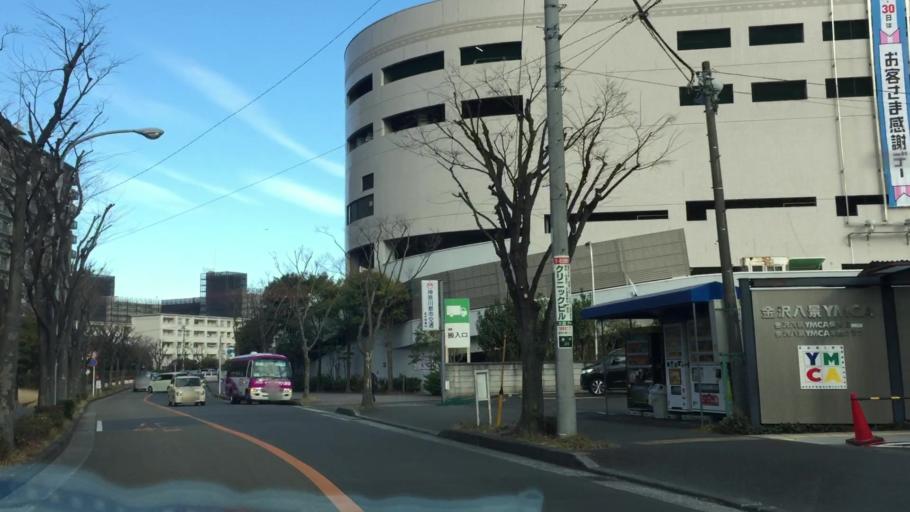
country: JP
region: Kanagawa
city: Zushi
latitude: 35.3339
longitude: 139.6213
